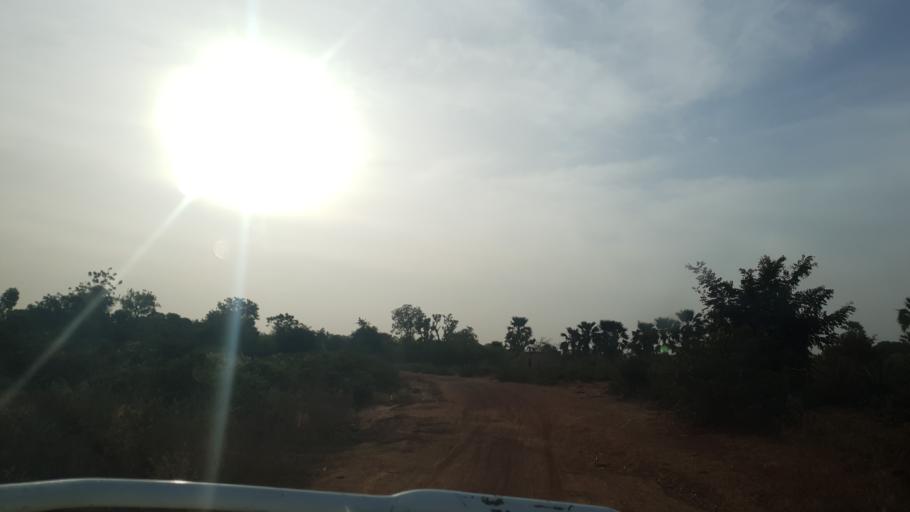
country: ML
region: Segou
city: Baroueli
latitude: 12.7717
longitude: -6.9347
